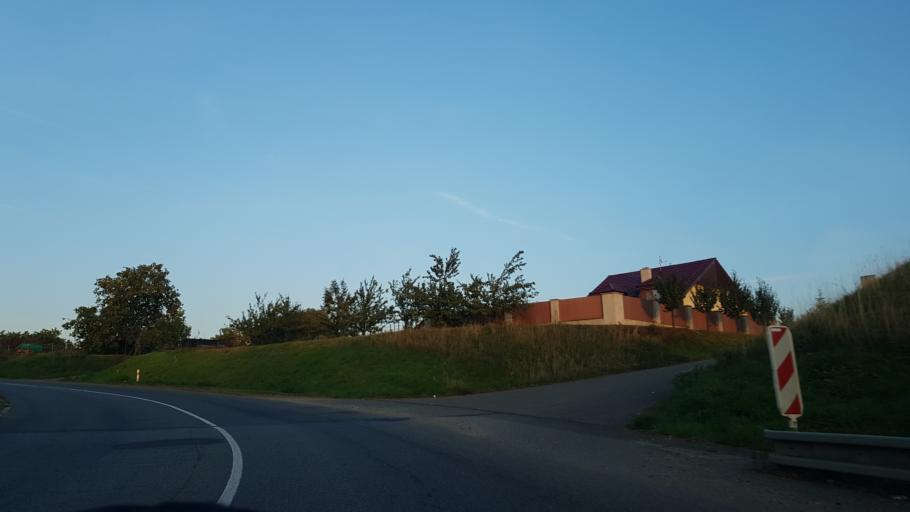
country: CZ
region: Zlin
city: Nedakonice
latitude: 49.0290
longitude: 17.3715
